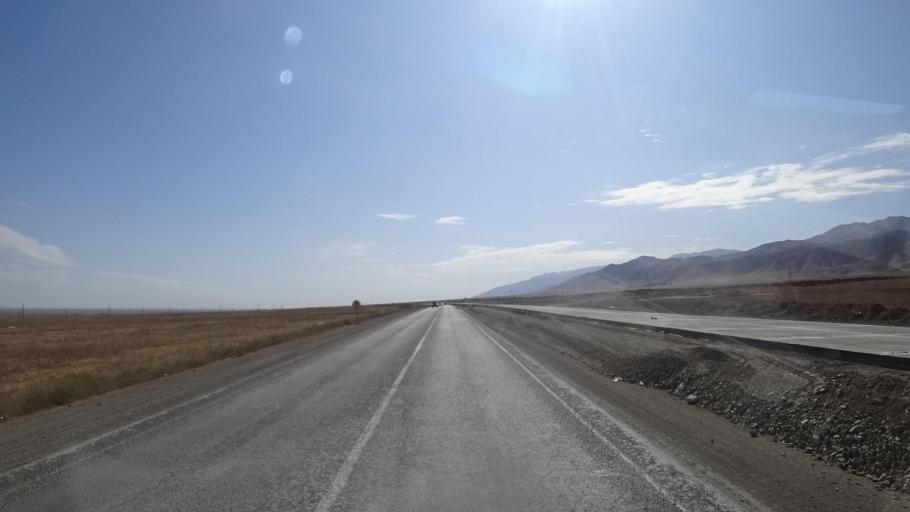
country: KG
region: Chuy
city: Ivanovka
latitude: 43.3890
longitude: 75.1460
